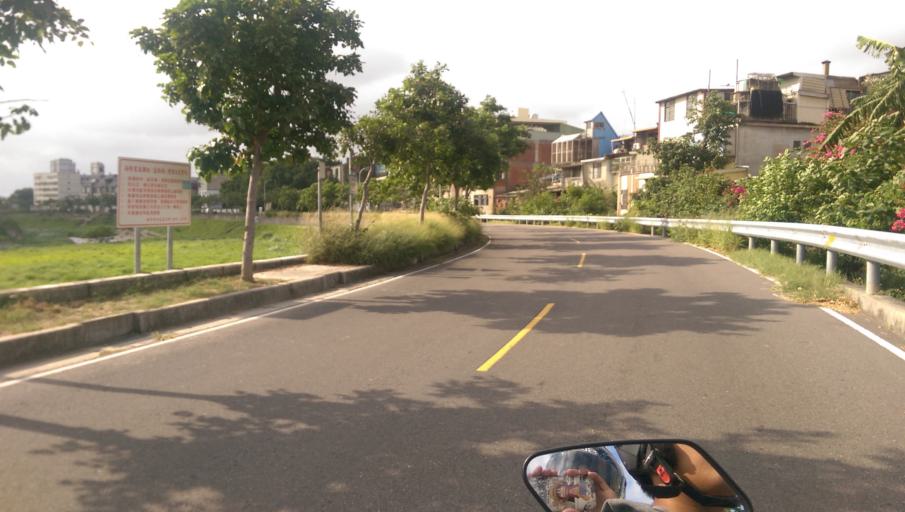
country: TW
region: Taiwan
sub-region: Hsinchu
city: Hsinchu
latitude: 24.8044
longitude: 120.9452
